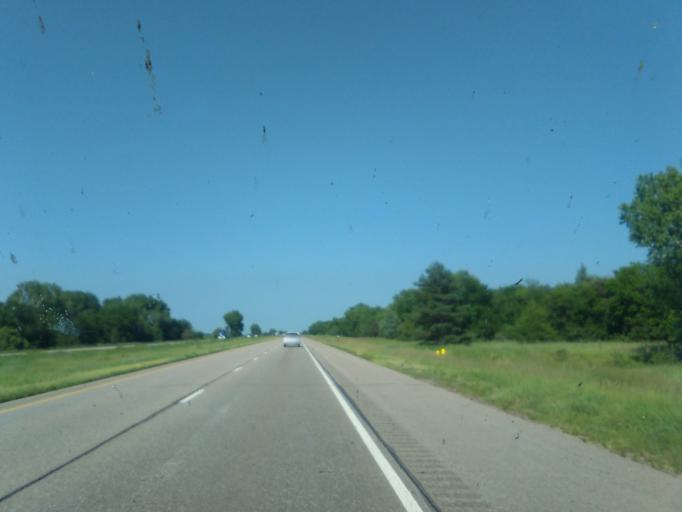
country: US
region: Nebraska
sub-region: Hall County
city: Wood River
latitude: 40.7751
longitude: -98.5503
